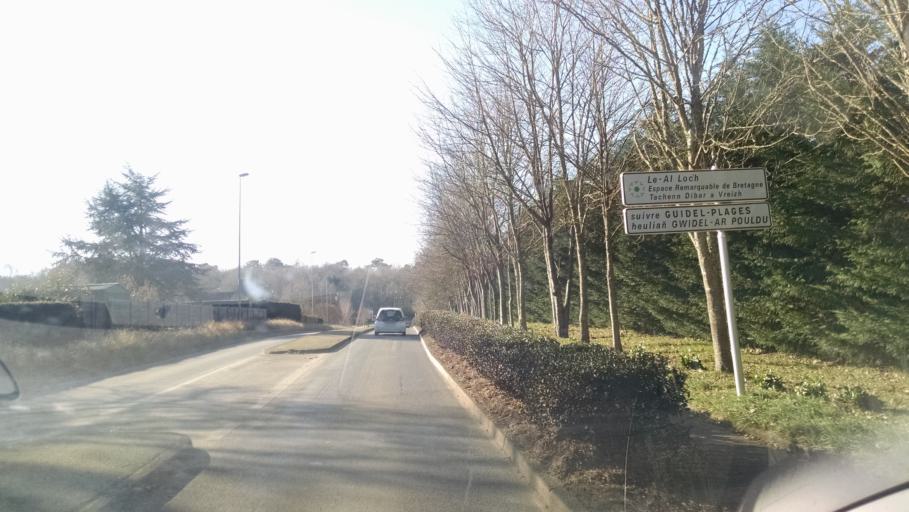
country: FR
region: Brittany
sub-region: Departement du Morbihan
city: Gestel
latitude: 47.7990
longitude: -3.4793
